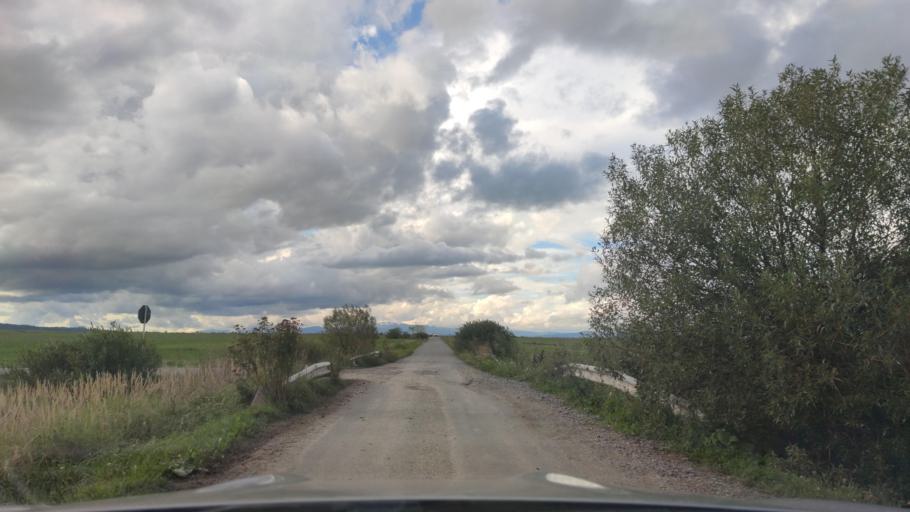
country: RO
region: Harghita
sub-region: Comuna Remetea
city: Remetea
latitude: 46.8159
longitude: 25.4395
